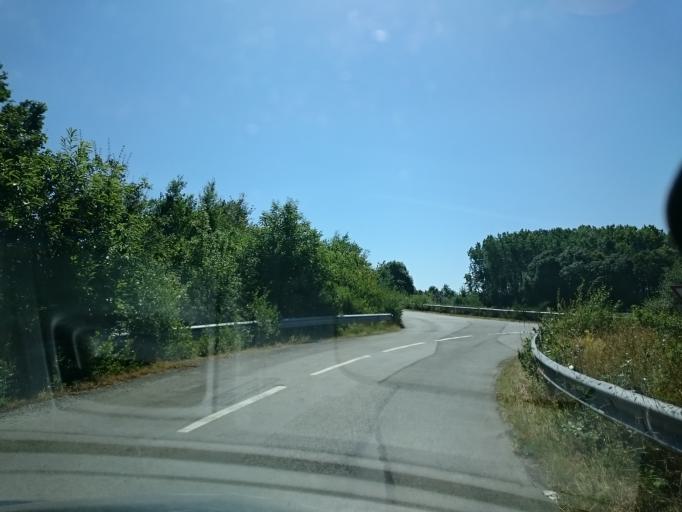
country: FR
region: Brittany
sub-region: Departement d'Ille-et-Vilaine
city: Vern-sur-Seiche
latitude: 48.0357
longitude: -1.6030
